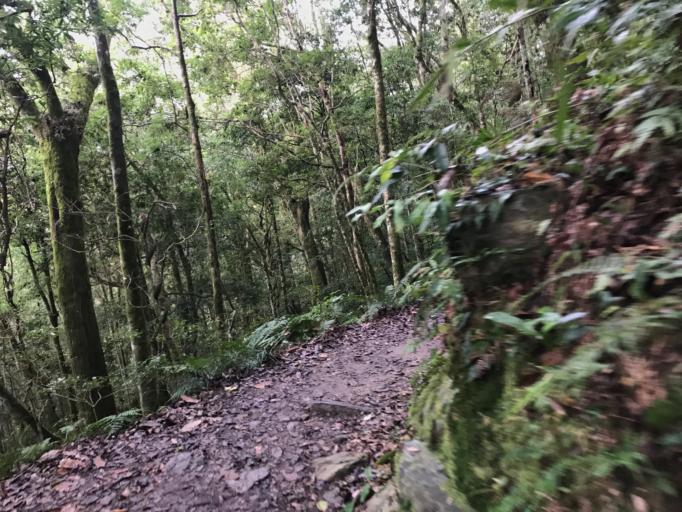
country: TW
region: Taiwan
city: Daxi
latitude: 24.5502
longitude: 121.2917
